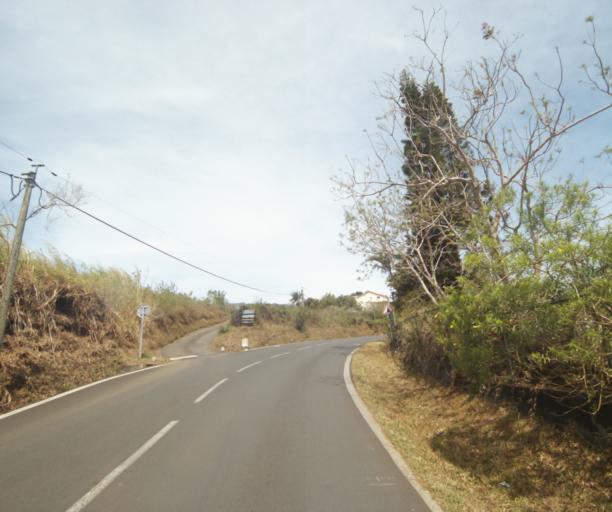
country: RE
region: Reunion
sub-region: Reunion
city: Saint-Paul
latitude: -21.0426
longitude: 55.3068
